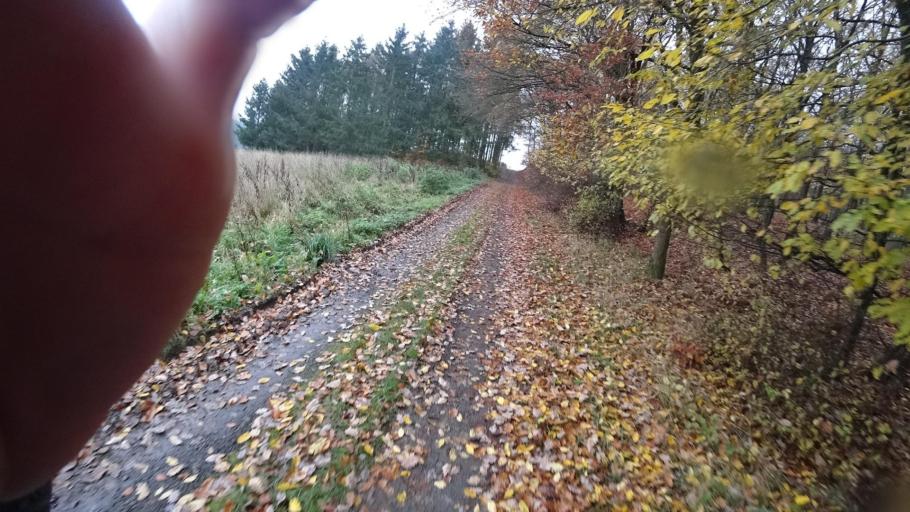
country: DE
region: Rheinland-Pfalz
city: Bad Neuenahr-Ahrweiler
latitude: 50.4980
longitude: 7.0951
